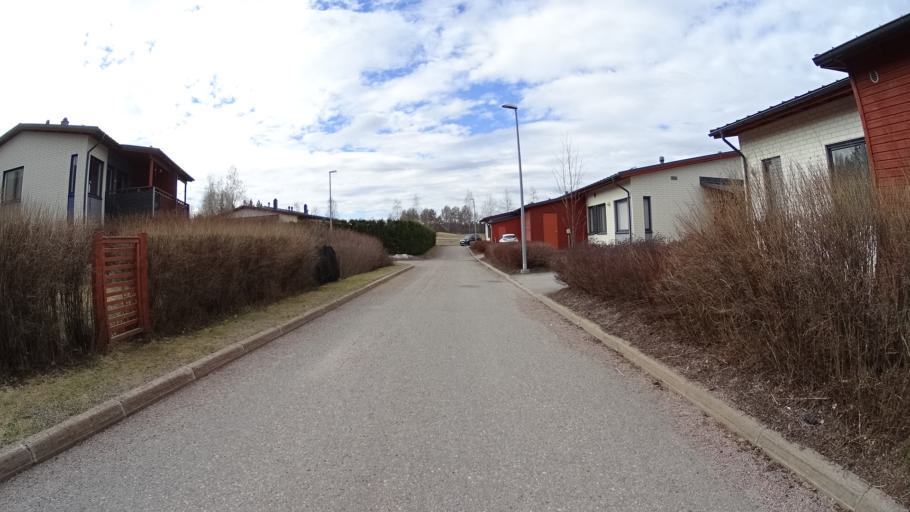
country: FI
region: Uusimaa
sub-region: Helsinki
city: Kauniainen
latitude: 60.2730
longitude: 24.7460
